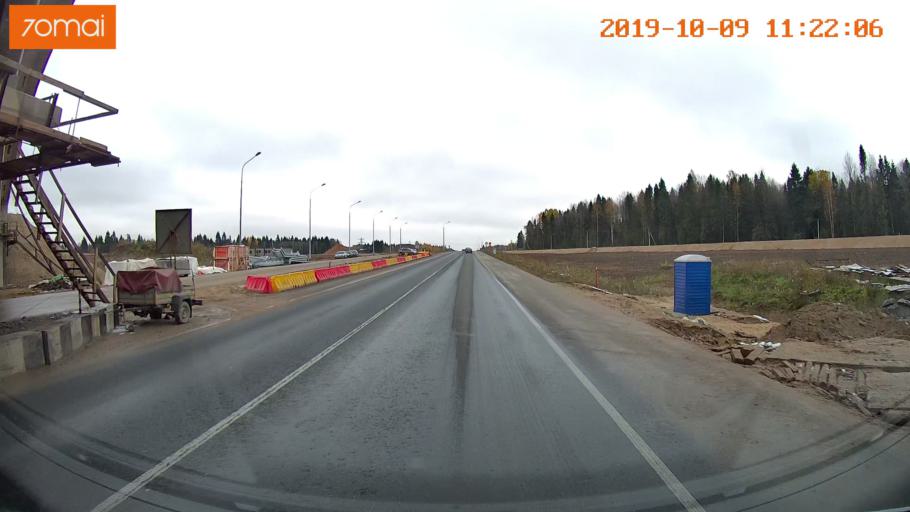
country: RU
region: Vologda
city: Vologda
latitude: 59.1345
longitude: 39.9549
